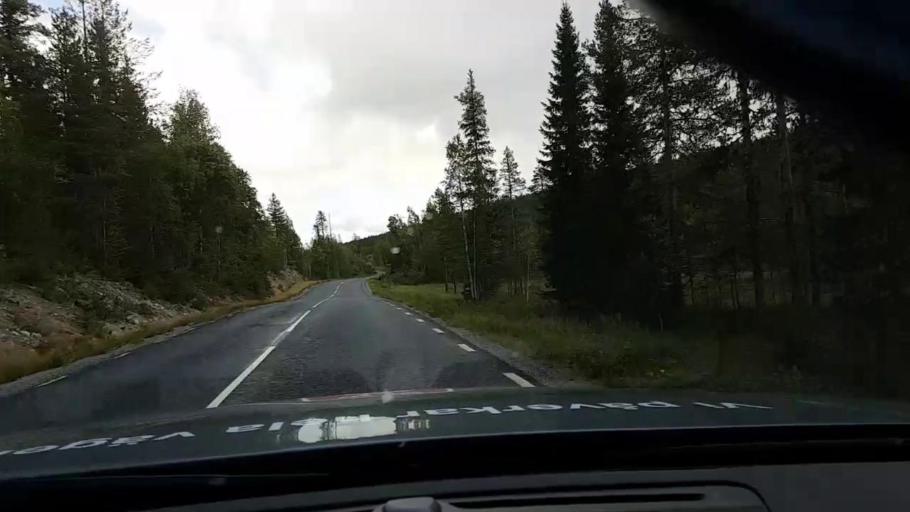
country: SE
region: Vaesterbotten
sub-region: Asele Kommun
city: Asele
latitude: 63.8331
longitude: 17.4493
